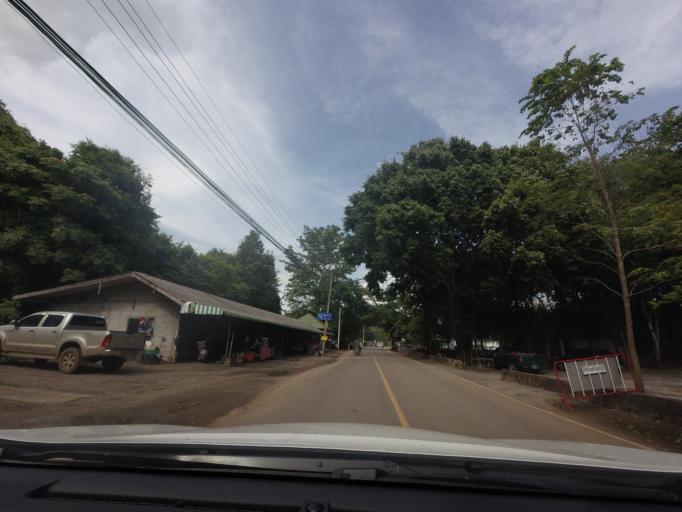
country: TH
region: Nakhon Ratchasima
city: Pak Chong
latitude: 14.5482
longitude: 101.4201
